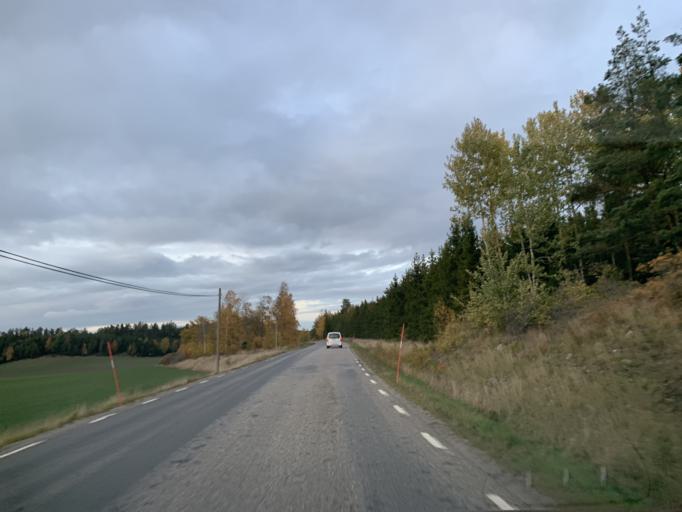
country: SE
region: Stockholm
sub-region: Nynashamns Kommun
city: Osmo
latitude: 58.9449
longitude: 17.7617
